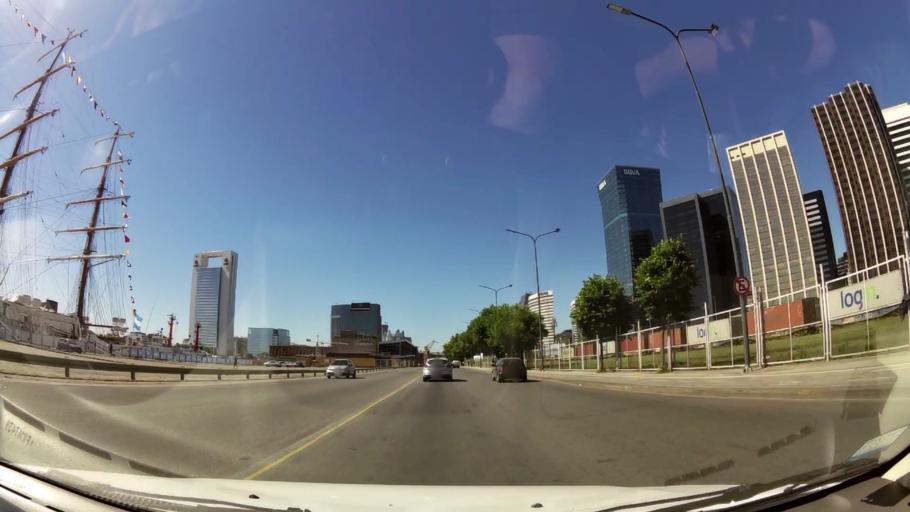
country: AR
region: Buenos Aires F.D.
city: Retiro
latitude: -34.5947
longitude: -58.3694
